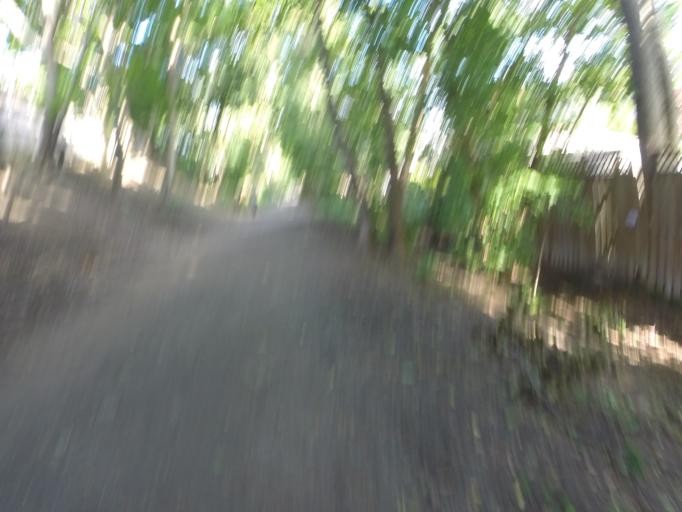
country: CA
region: Ontario
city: Toronto
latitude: 43.7002
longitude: -79.4117
